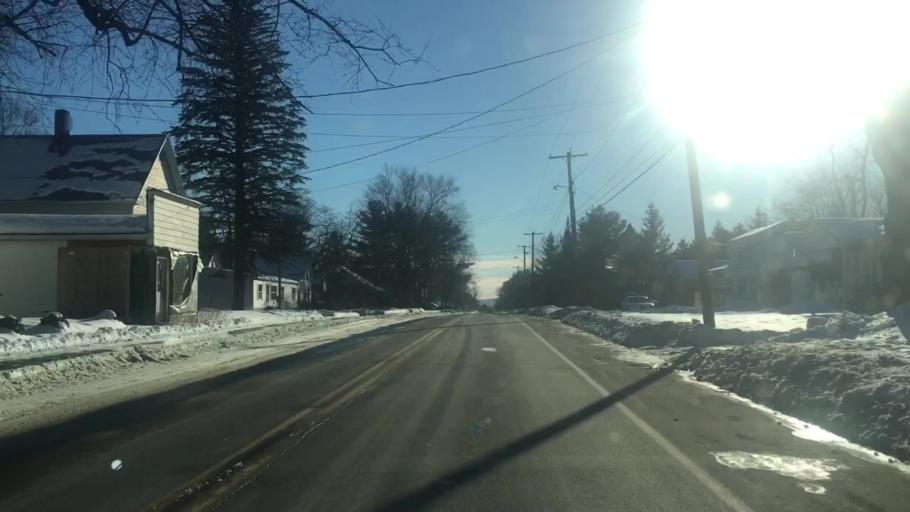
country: US
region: Maine
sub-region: Somerset County
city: Madison
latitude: 44.7889
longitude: -69.8827
